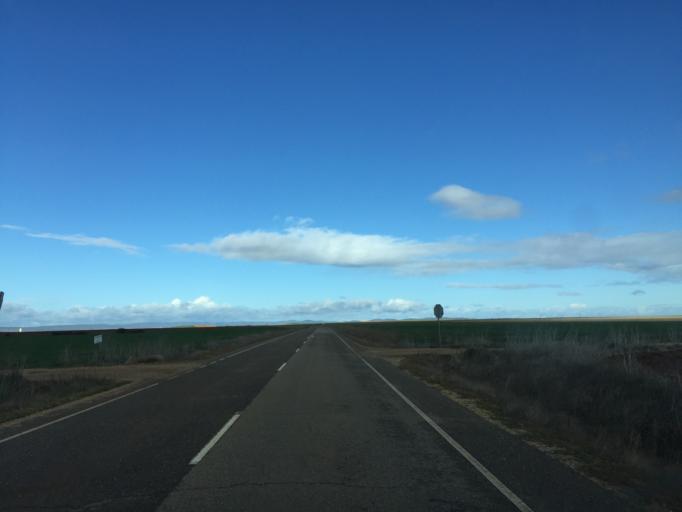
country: ES
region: Castille and Leon
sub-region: Provincia de Zamora
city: Manganeses de la Lampreana
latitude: 41.7576
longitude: -5.7250
